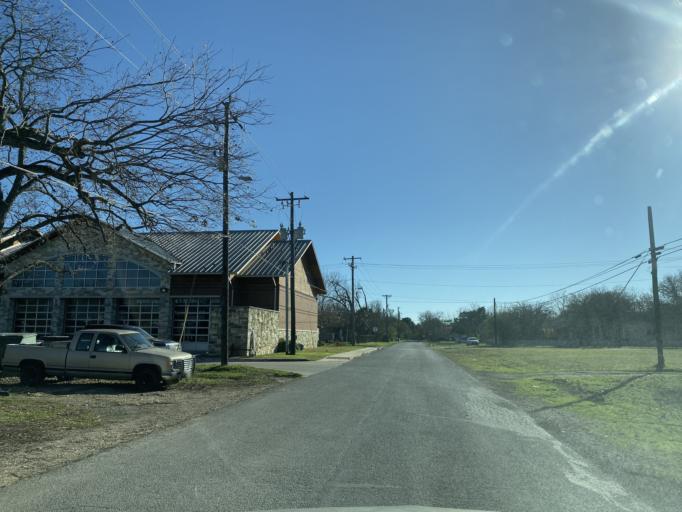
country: US
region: Texas
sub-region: Hays County
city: Kyle
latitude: 29.9877
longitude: -97.8775
